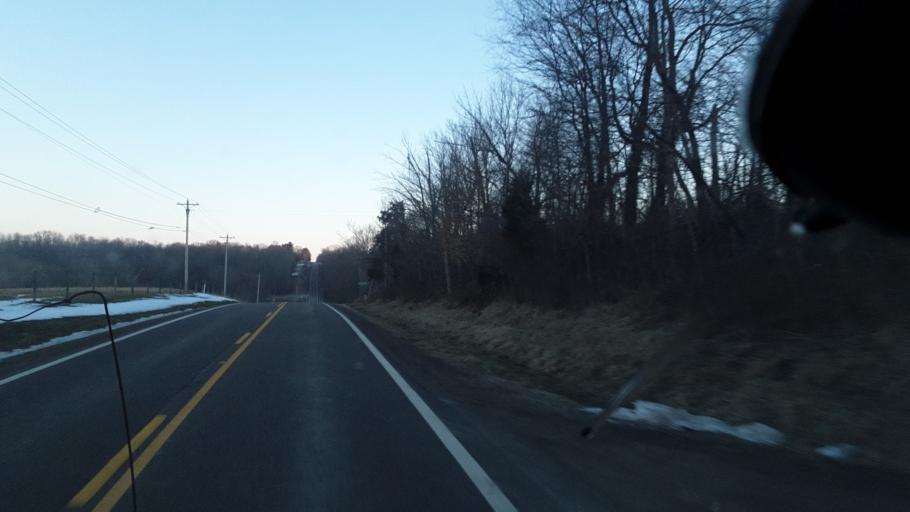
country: US
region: Ohio
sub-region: Perry County
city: Somerset
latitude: 39.7619
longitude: -82.3040
